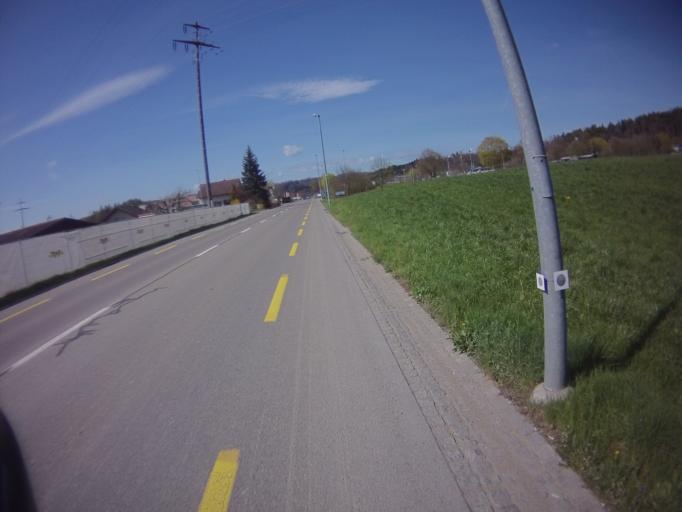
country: CH
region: Aargau
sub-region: Bezirk Baden
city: Niederrohrdorf
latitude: 47.4420
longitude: 8.2959
